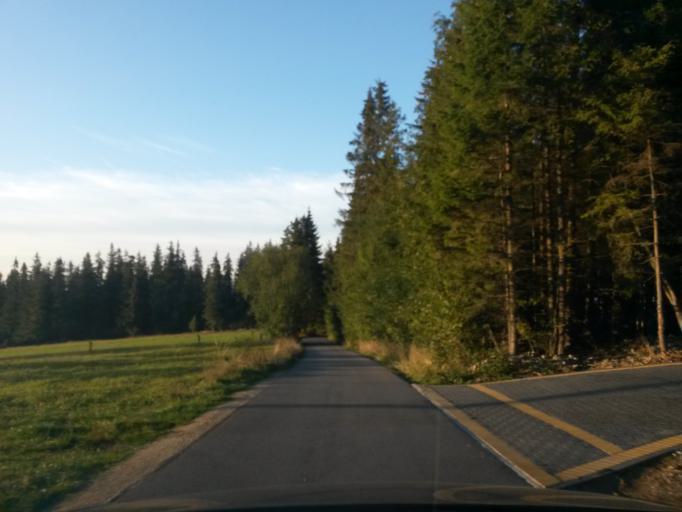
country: PL
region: Lesser Poland Voivodeship
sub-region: Powiat tatrzanski
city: Koscielisko
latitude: 49.3160
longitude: 19.9038
